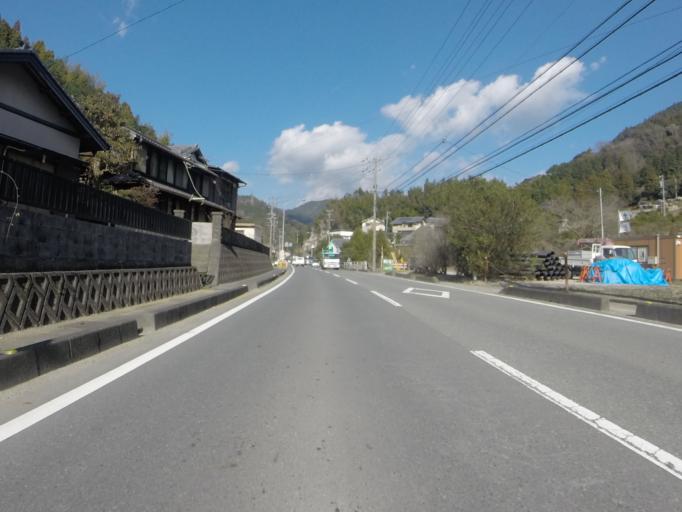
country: JP
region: Shizuoka
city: Fujinomiya
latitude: 35.1157
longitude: 138.5127
